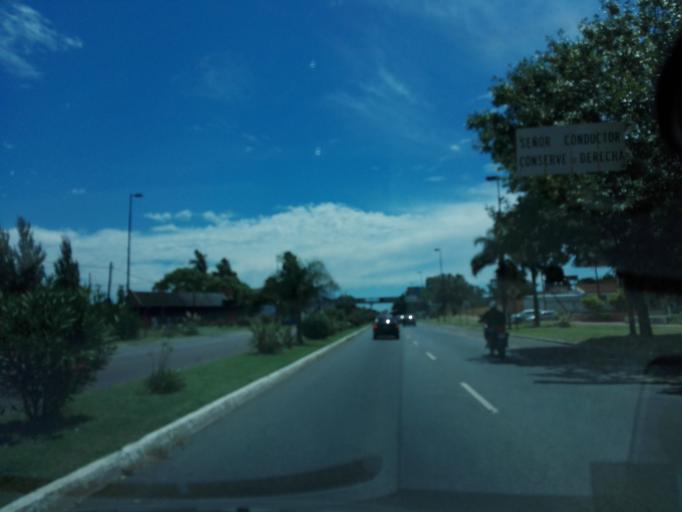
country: AR
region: Buenos Aires
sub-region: Partido de La Plata
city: La Plata
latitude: -34.8898
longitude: -57.9971
